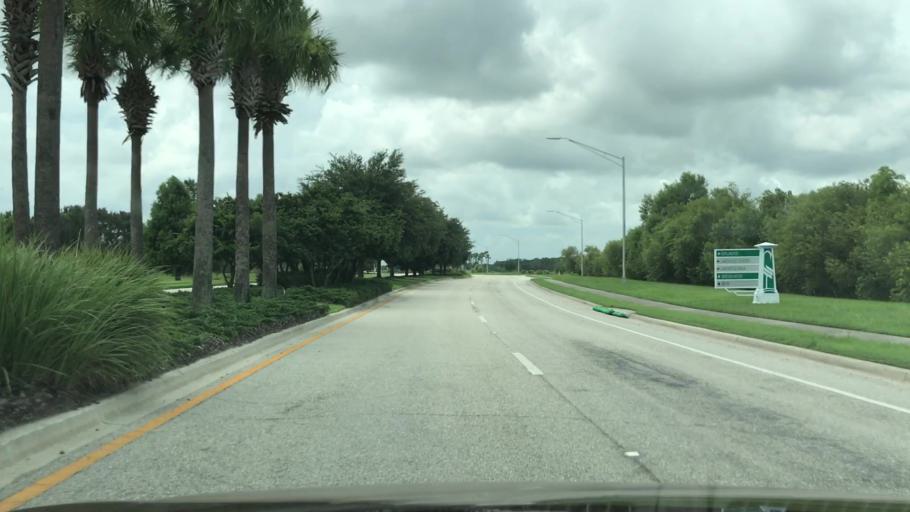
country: US
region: Florida
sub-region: Sarasota County
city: The Meadows
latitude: 27.4463
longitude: -82.4158
